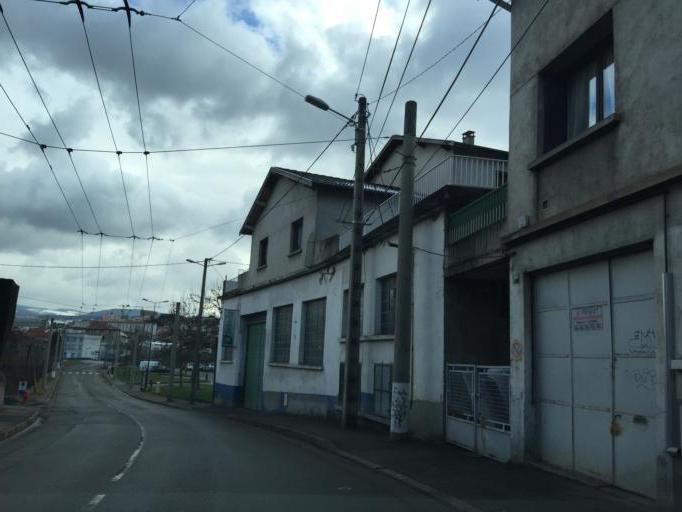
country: FR
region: Rhone-Alpes
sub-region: Departement de la Loire
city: Saint-Etienne
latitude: 45.4400
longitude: 4.3761
